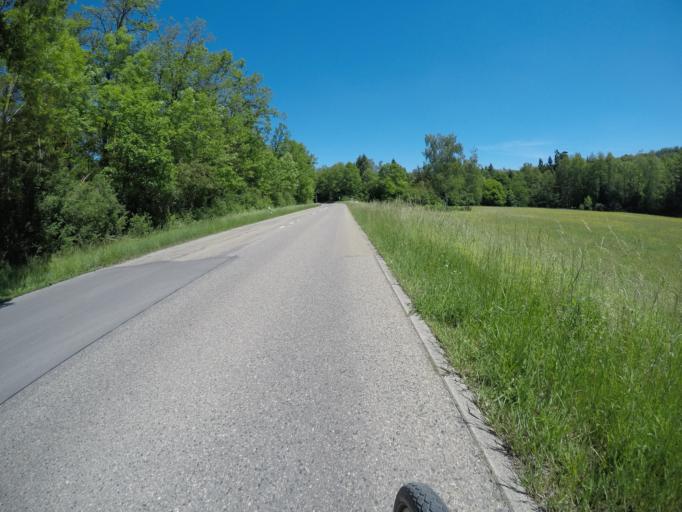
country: DE
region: Baden-Wuerttemberg
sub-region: Regierungsbezirk Stuttgart
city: Sindelfingen
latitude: 48.7438
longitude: 9.0154
